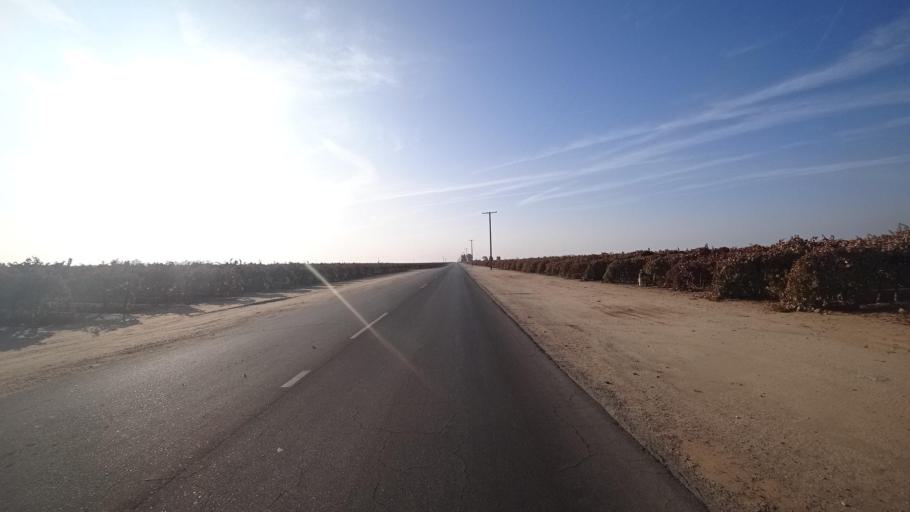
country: US
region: California
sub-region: Kern County
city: Delano
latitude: 35.7553
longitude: -119.1874
